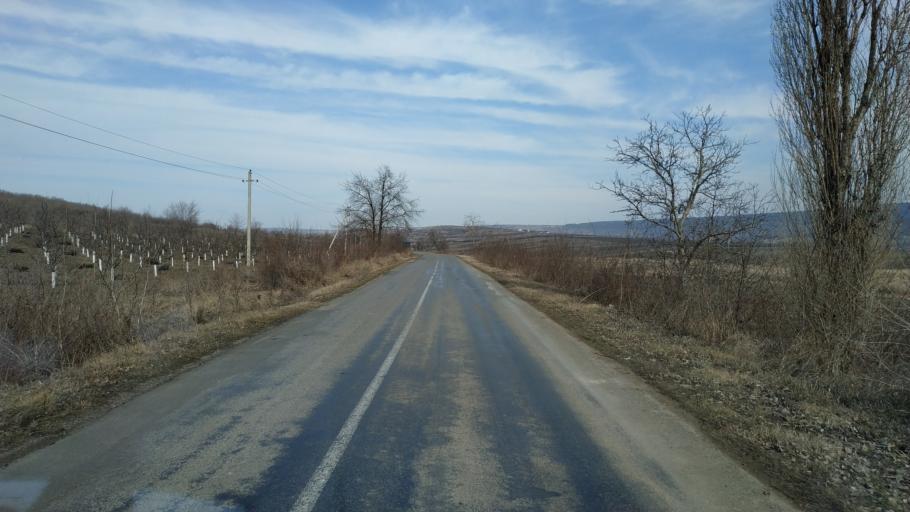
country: MD
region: Nisporeni
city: Nisporeni
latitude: 47.1269
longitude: 28.1215
